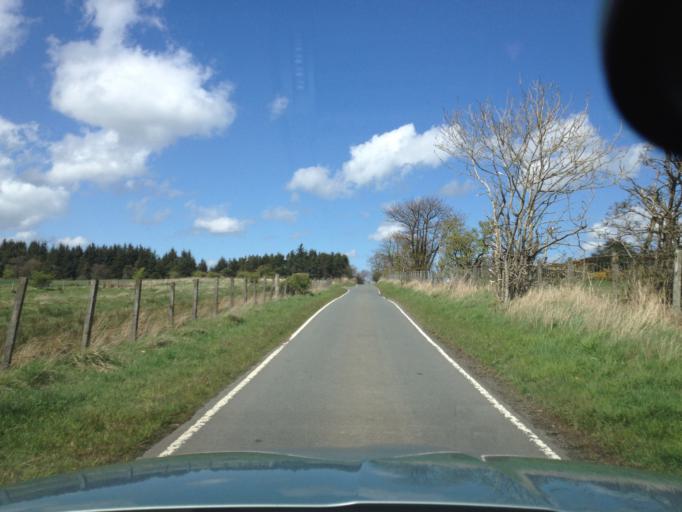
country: GB
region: Scotland
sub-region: West Lothian
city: Linlithgow
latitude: 55.9409
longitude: -3.5863
